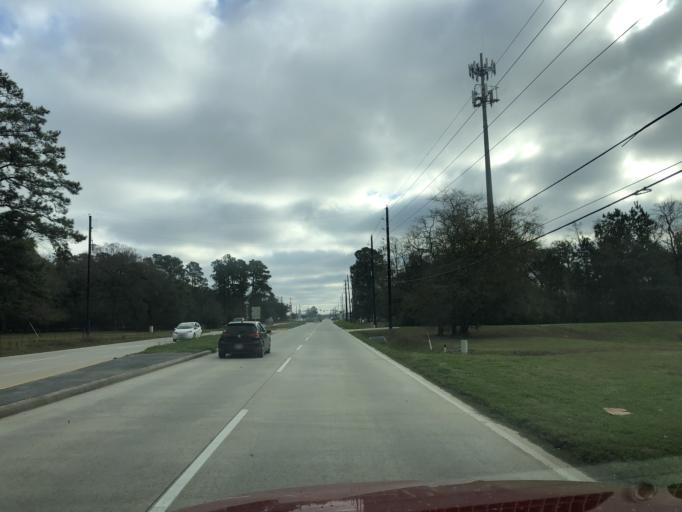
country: US
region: Texas
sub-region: Harris County
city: Spring
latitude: 30.0828
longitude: -95.4548
